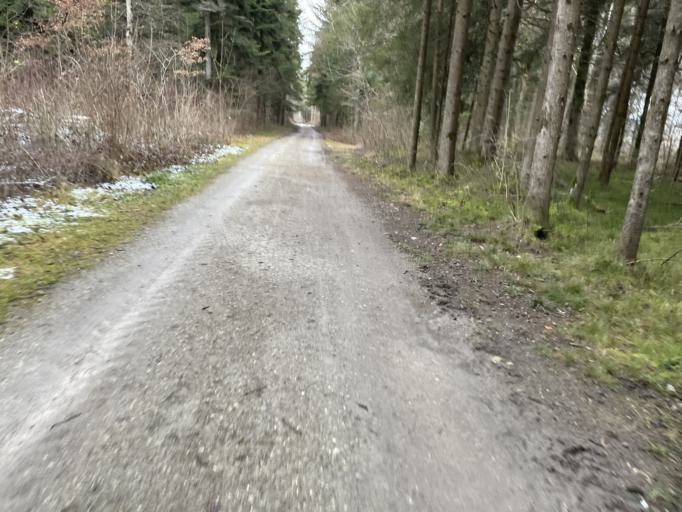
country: CH
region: Bern
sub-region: Bern-Mittelland District
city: Niederwichtrach
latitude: 46.8495
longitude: 7.5576
